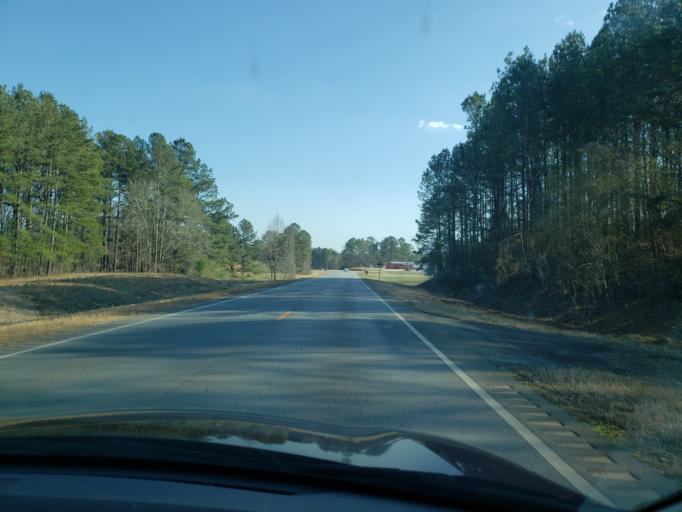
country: US
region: Alabama
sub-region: Randolph County
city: Wedowee
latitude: 33.4180
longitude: -85.5487
